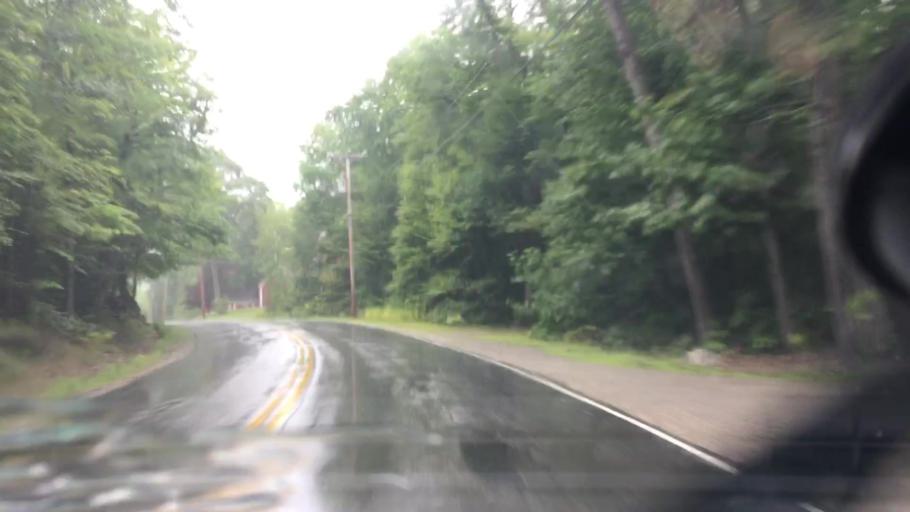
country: US
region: Maine
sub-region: Oxford County
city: Lovell
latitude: 44.2583
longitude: -70.8334
